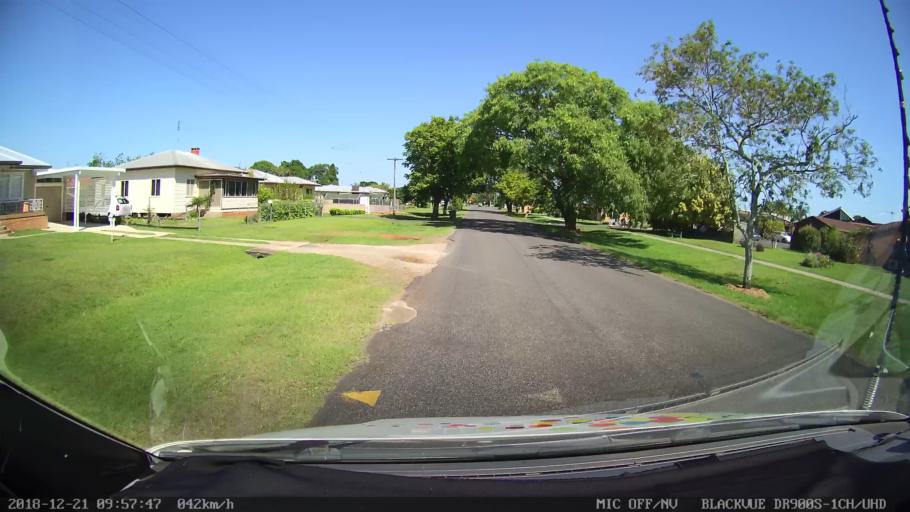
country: AU
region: New South Wales
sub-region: Clarence Valley
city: Grafton
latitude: -29.6736
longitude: 152.9374
